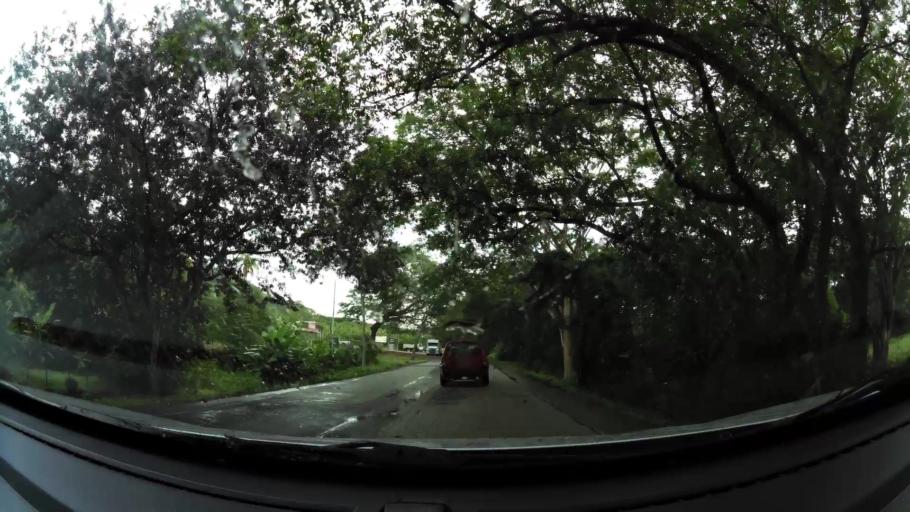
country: CR
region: Guanacaste
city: Juntas
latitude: 10.2204
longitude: -84.9736
